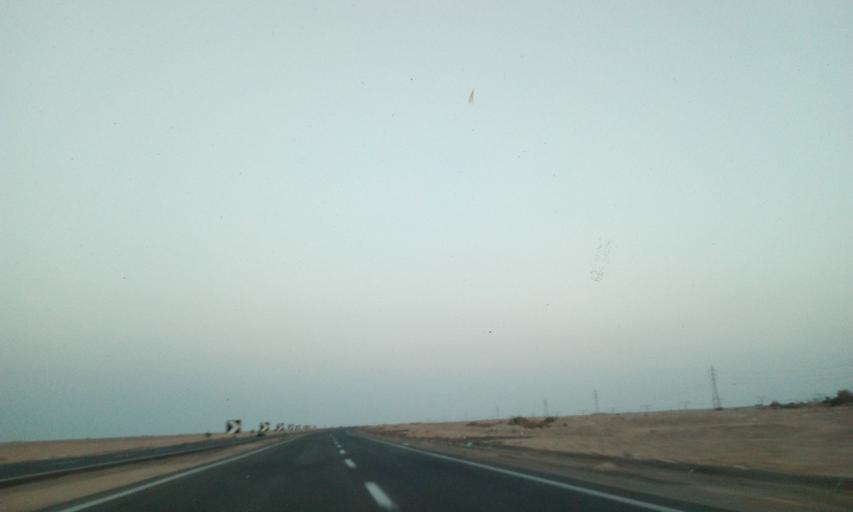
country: EG
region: Red Sea
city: El Gouna
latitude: 27.3577
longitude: 33.6444
